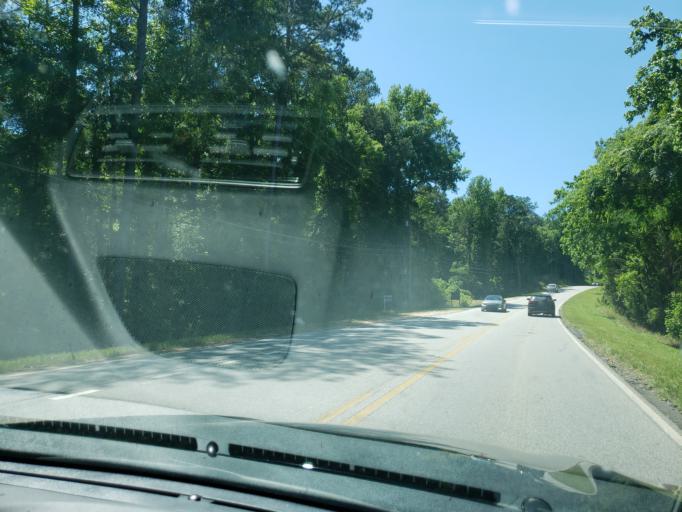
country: US
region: Alabama
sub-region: Lee County
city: Auburn
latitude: 32.6460
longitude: -85.4818
